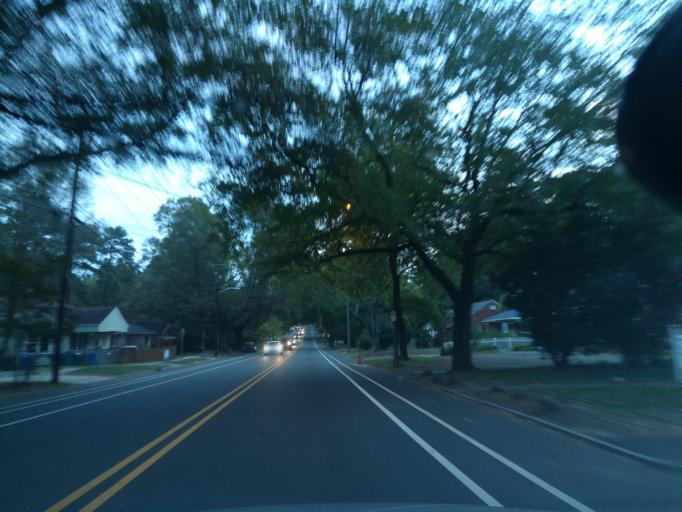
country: US
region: North Carolina
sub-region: Durham County
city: Durham
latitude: 36.0225
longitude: -78.9188
